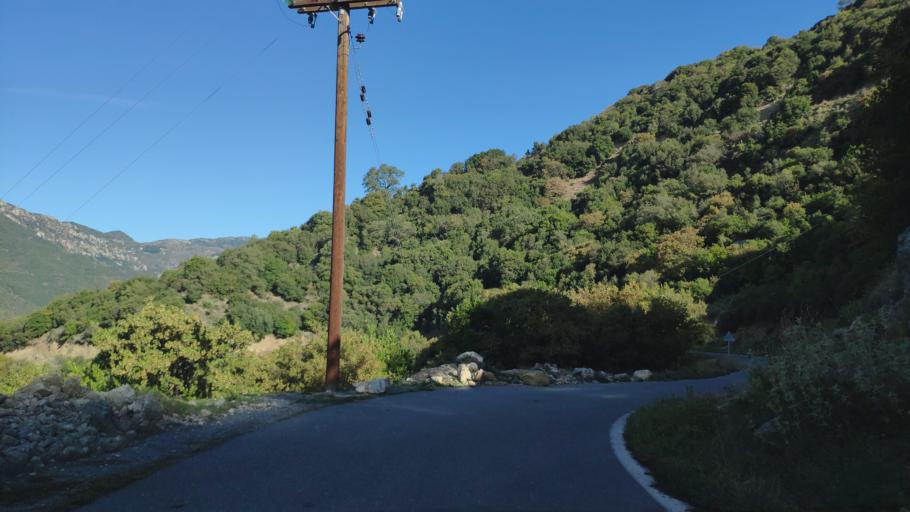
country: GR
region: Peloponnese
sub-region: Nomos Arkadias
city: Dimitsana
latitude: 37.5497
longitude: 22.0593
